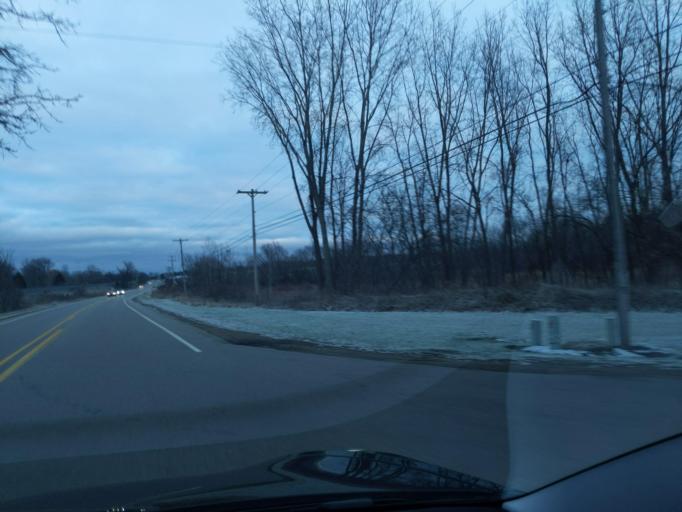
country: US
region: Michigan
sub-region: Jackson County
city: Spring Arbor
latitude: 42.2546
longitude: -84.4902
